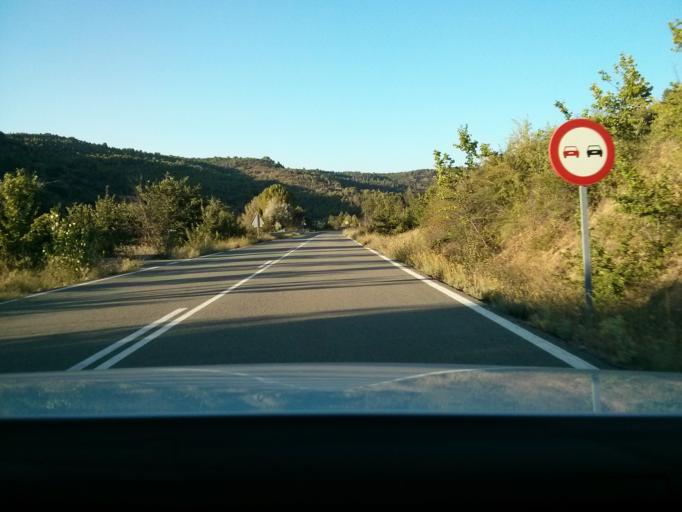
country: ES
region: Castille-La Mancha
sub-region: Provincia de Guadalajara
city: Mantiel
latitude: 40.6300
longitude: -2.6582
